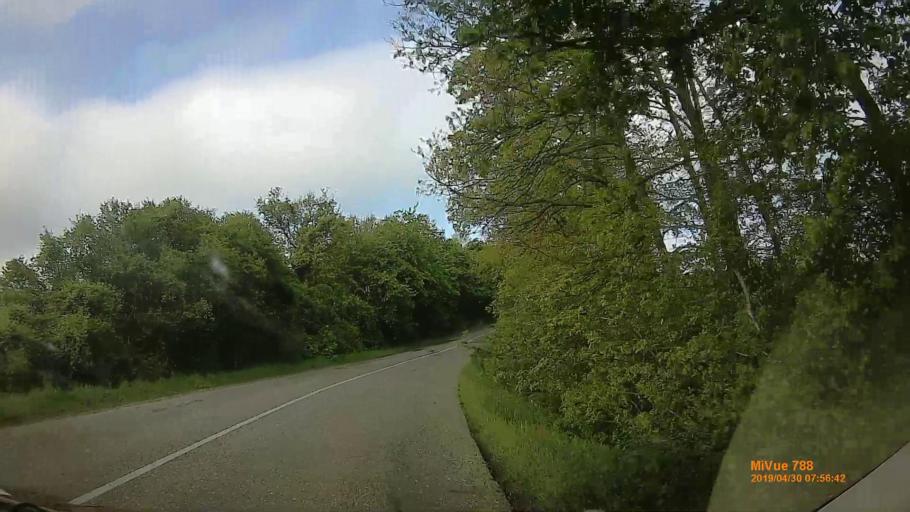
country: HU
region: Nograd
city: Retsag
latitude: 47.8819
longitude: 19.1110
